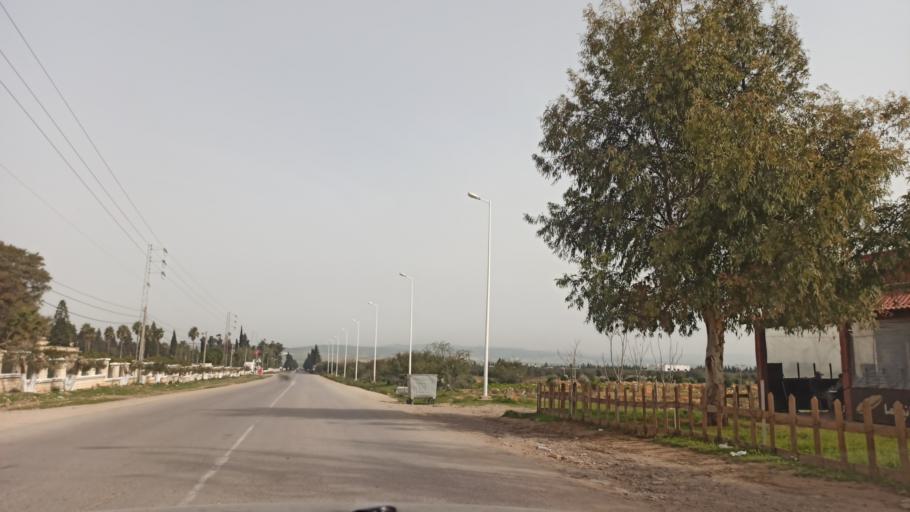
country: TN
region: Zaghwan
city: Zaghouan
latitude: 36.4245
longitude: 10.0940
